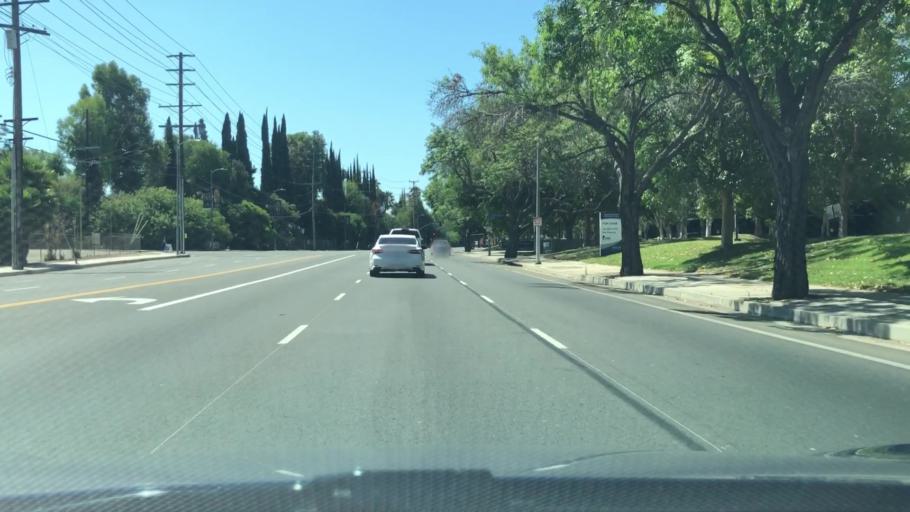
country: US
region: California
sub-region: Los Angeles County
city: Woodland Hills
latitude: 34.1753
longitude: -118.5890
